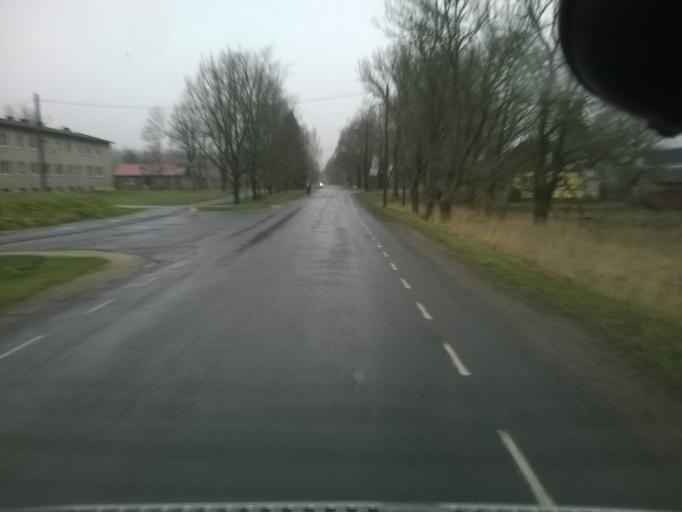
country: EE
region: Raplamaa
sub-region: Kohila vald
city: Kohila
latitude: 59.1610
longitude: 24.6506
